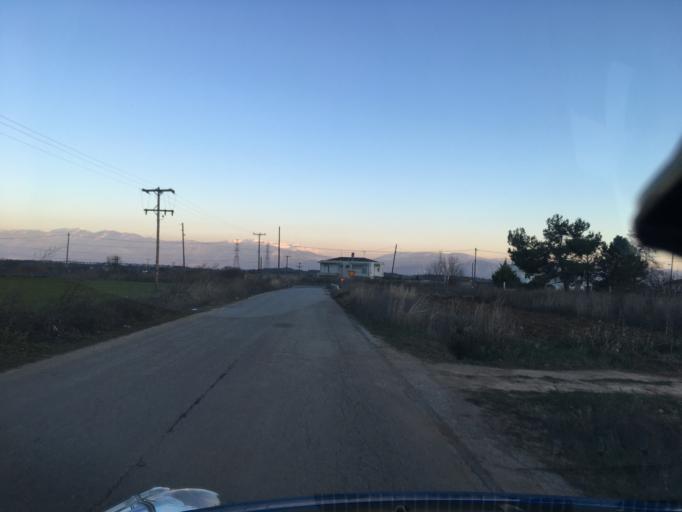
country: GR
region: West Macedonia
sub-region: Nomos Kozanis
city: Kozani
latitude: 40.2570
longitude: 21.7570
